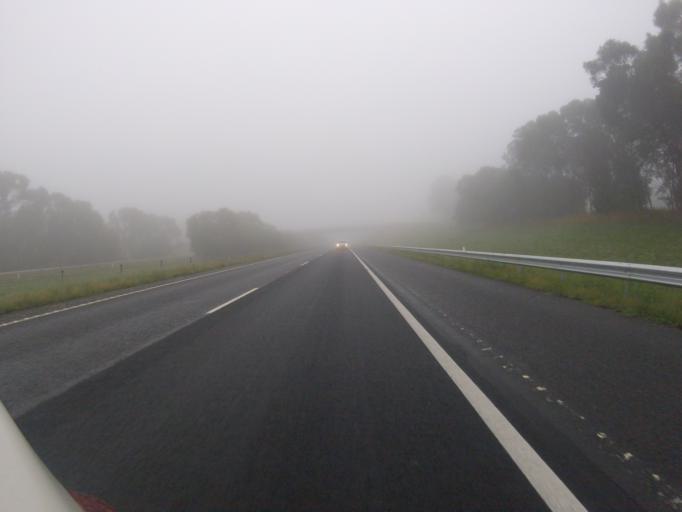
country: AU
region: Victoria
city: Brown Hill
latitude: -37.5498
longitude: 144.0532
